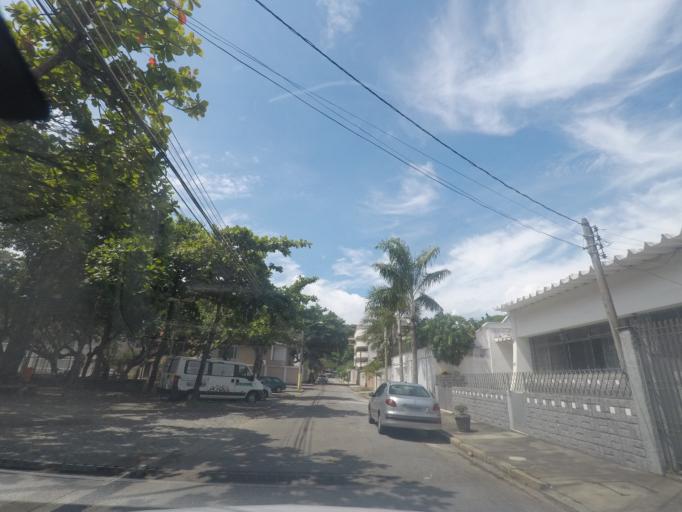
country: BR
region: Rio de Janeiro
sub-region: Rio De Janeiro
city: Rio de Janeiro
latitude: -22.8129
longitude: -43.2114
